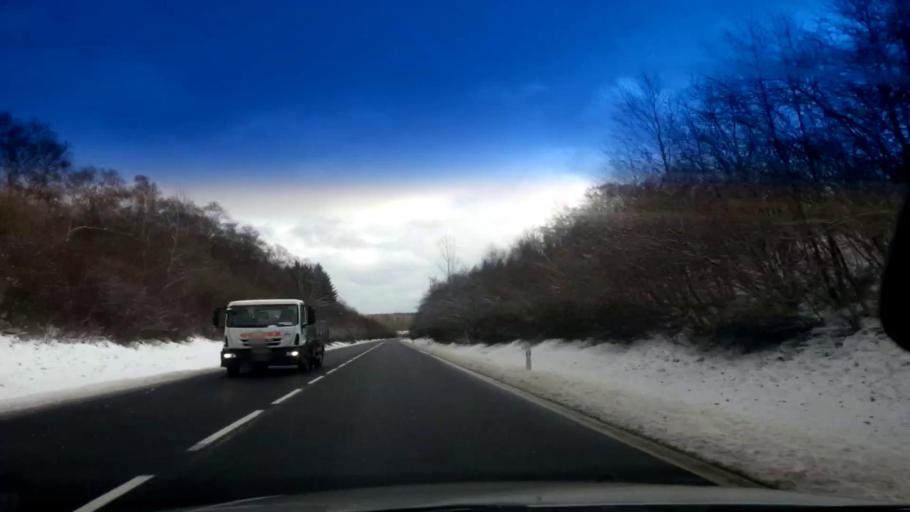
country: CZ
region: Karlovarsky
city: As
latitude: 50.2078
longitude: 12.1866
